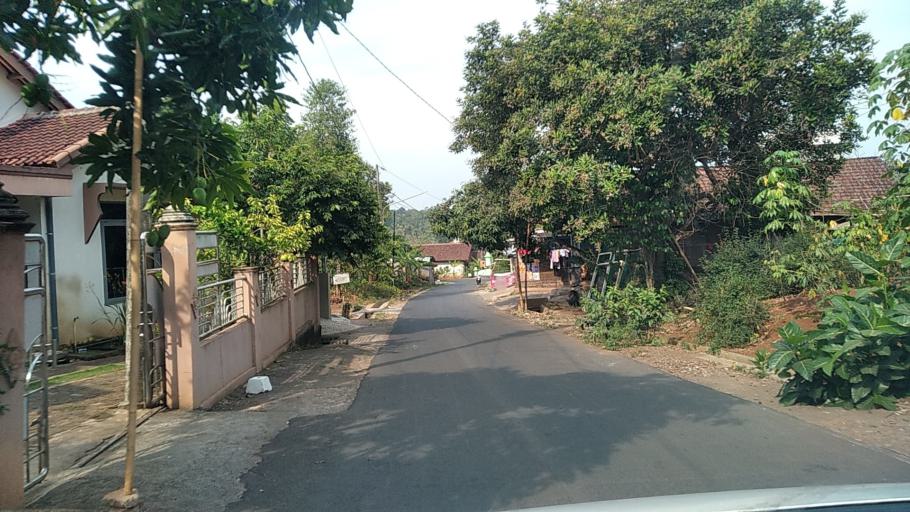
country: ID
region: Central Java
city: Ungaran
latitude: -7.0932
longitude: 110.3930
